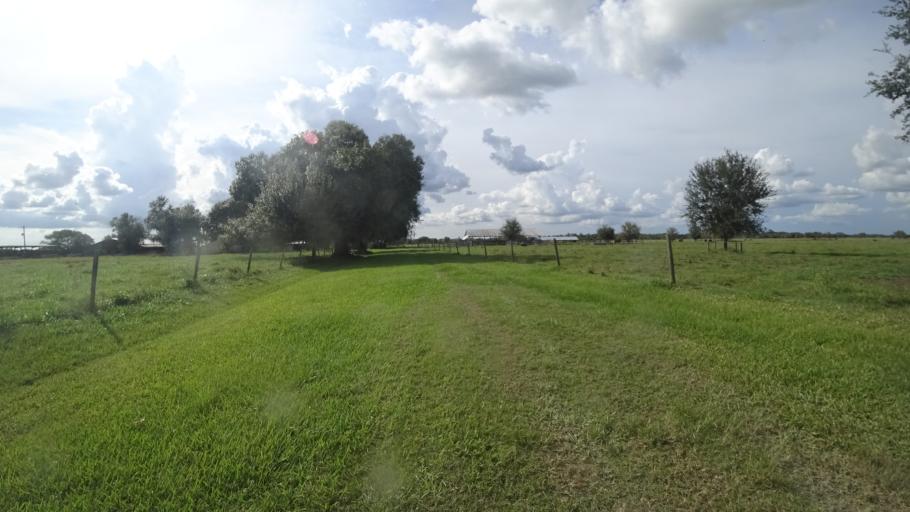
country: US
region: Florida
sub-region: Sarasota County
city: Lake Sarasota
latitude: 27.3319
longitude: -82.1811
